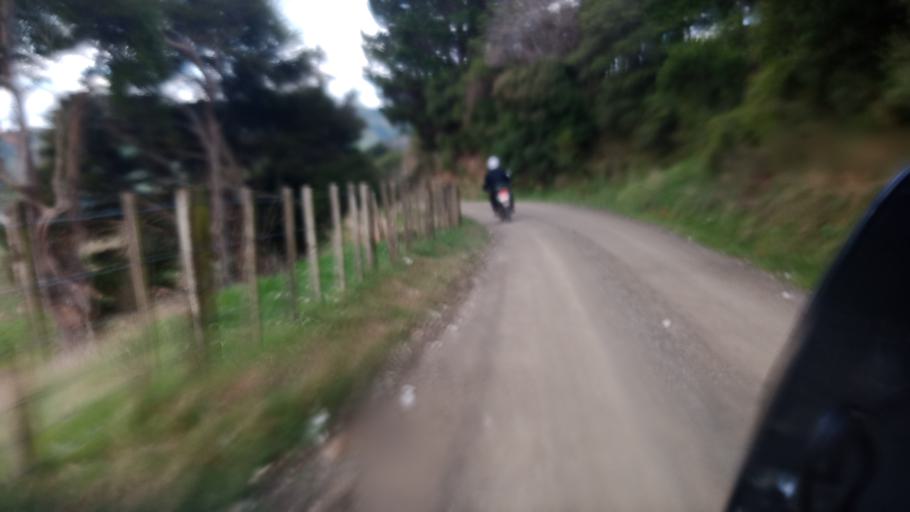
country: NZ
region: Gisborne
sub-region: Gisborne District
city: Gisborne
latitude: -38.4641
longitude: 177.6260
